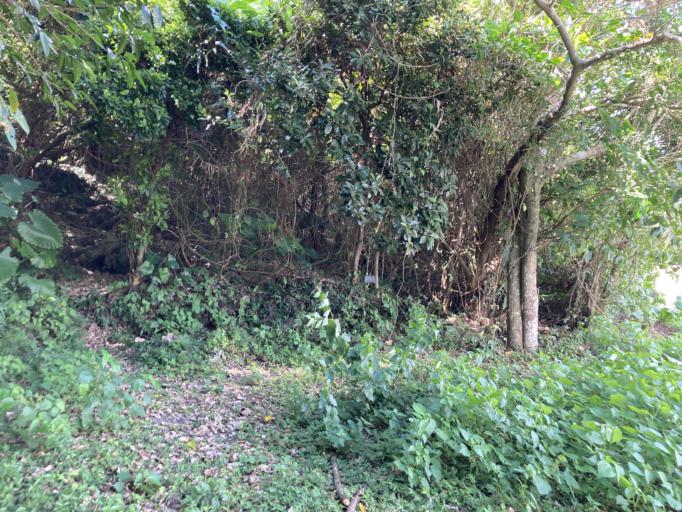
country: JP
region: Okinawa
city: Itoman
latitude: 26.1190
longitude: 127.7441
